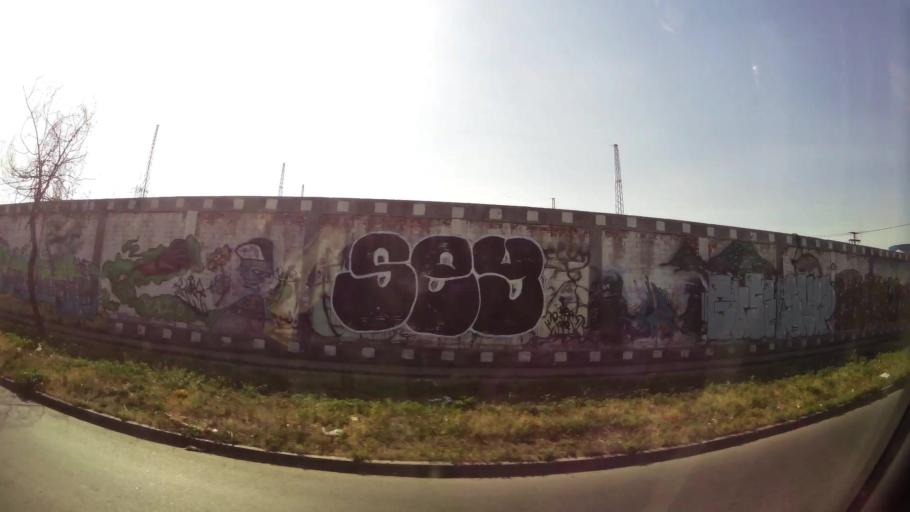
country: CL
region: Santiago Metropolitan
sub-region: Provincia de Santiago
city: Lo Prado
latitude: -33.4230
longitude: -70.7329
